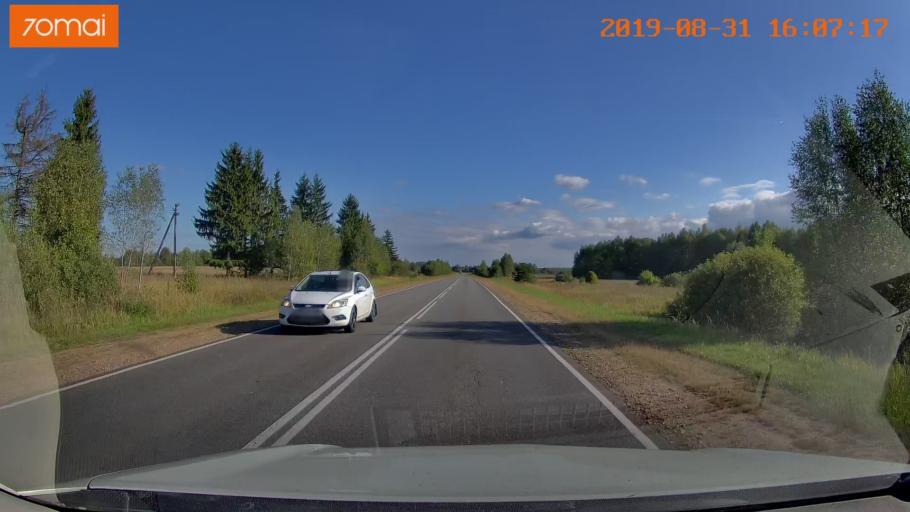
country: RU
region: Kaluga
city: Yukhnov
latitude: 54.6118
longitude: 35.3566
